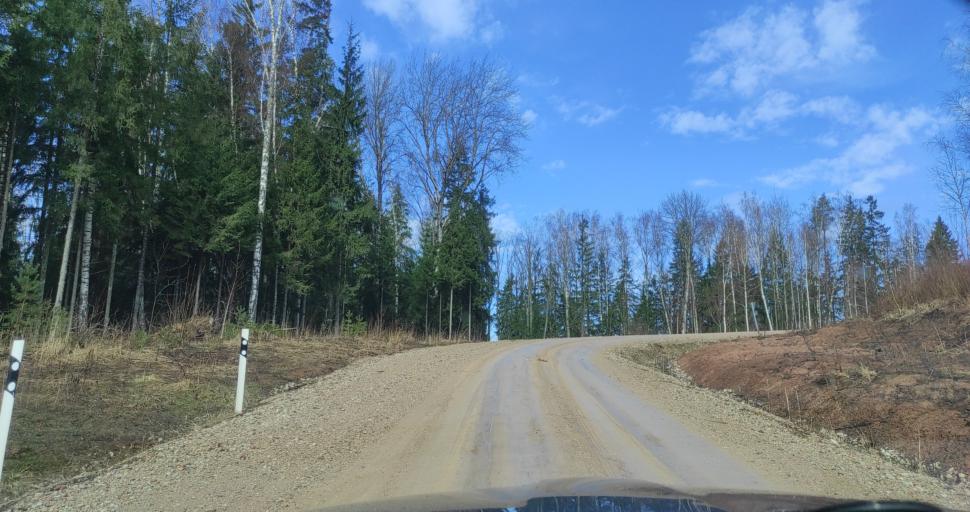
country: LV
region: Tukuma Rajons
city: Tukums
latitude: 57.1068
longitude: 23.0398
